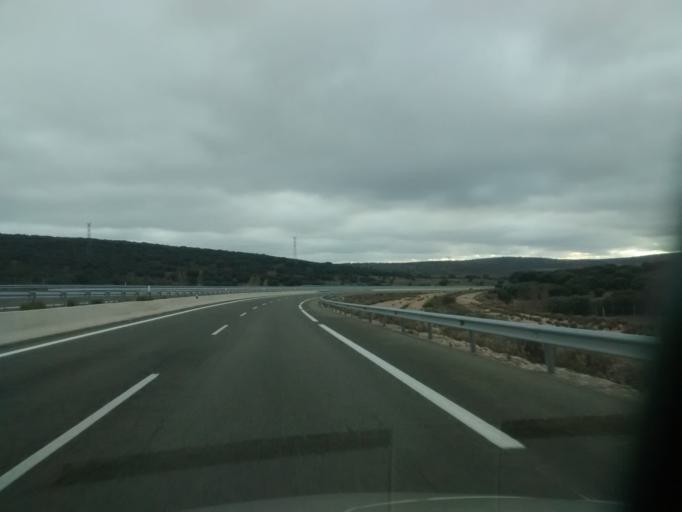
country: ES
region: Castille-La Mancha
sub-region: Provincia de Guadalajara
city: Sauca
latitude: 41.0229
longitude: -2.5186
